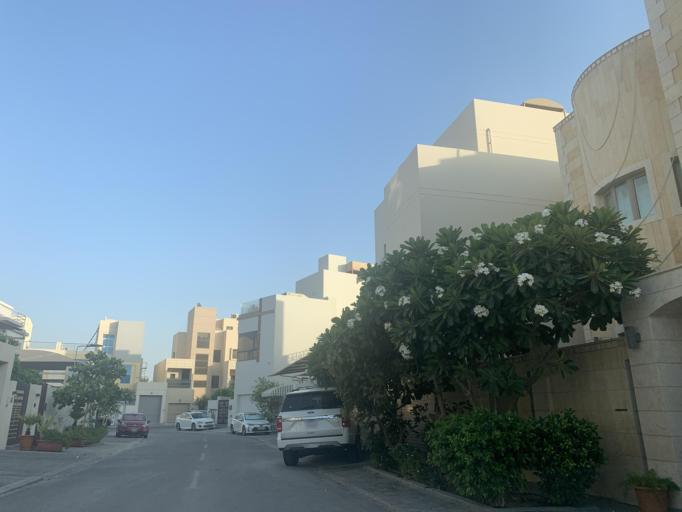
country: BH
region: Manama
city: Jidd Hafs
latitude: 26.1984
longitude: 50.5308
